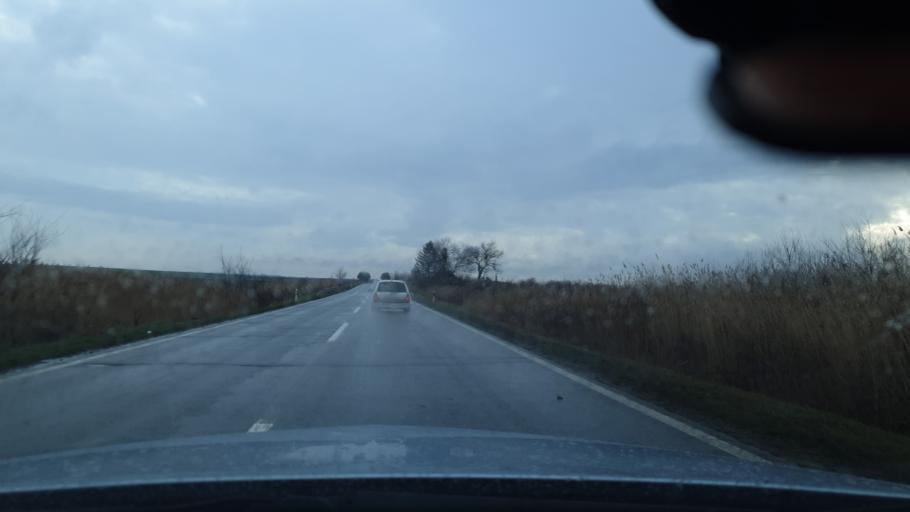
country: RS
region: Autonomna Pokrajina Vojvodina
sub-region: Juznobanatski Okrug
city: Kovin
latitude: 44.8342
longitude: 20.8202
